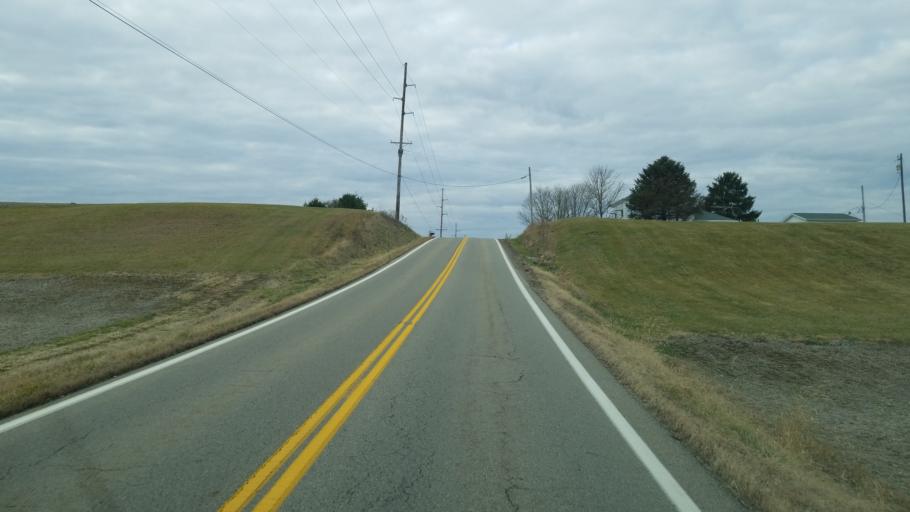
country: US
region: Ohio
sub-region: Ross County
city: Frankfort
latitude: 39.3558
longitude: -83.2649
